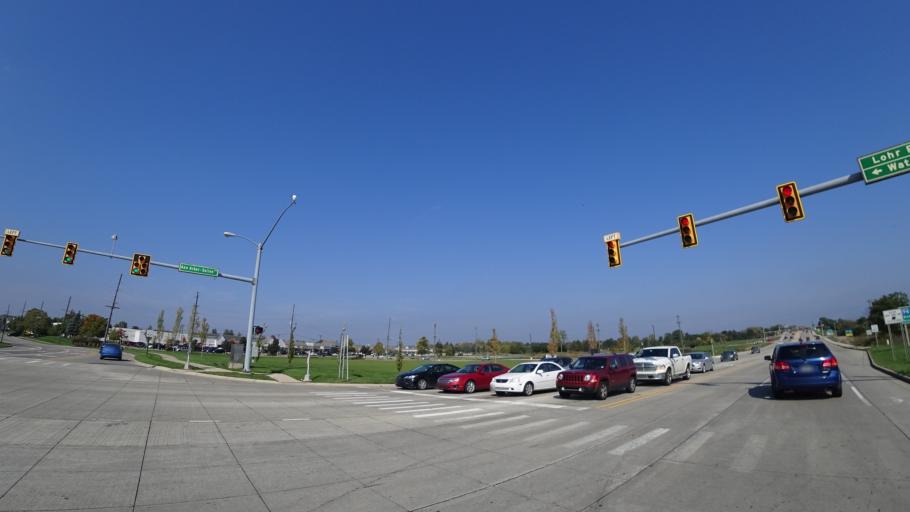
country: US
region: Michigan
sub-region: Washtenaw County
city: Ann Arbor
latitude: 42.2422
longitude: -83.7673
